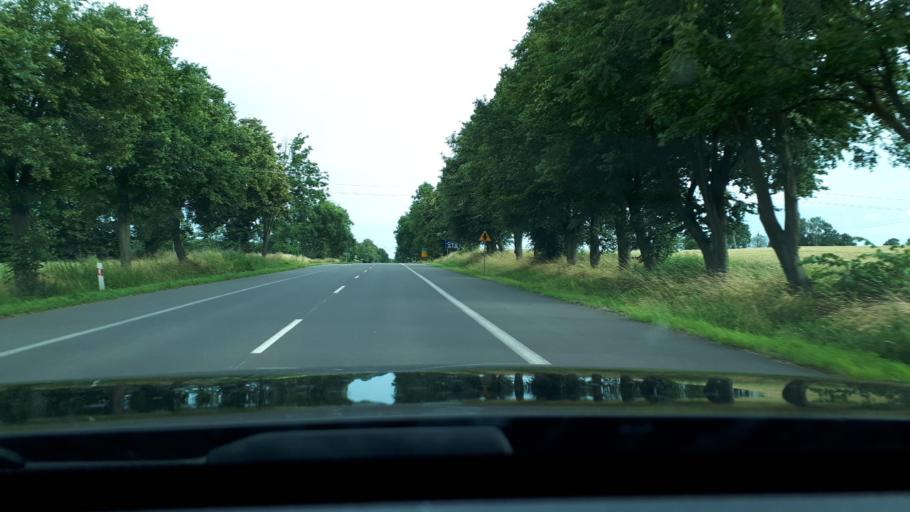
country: PL
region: Warmian-Masurian Voivodeship
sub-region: Powiat ostrodzki
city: Gierzwald
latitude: 53.6338
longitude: 20.0589
